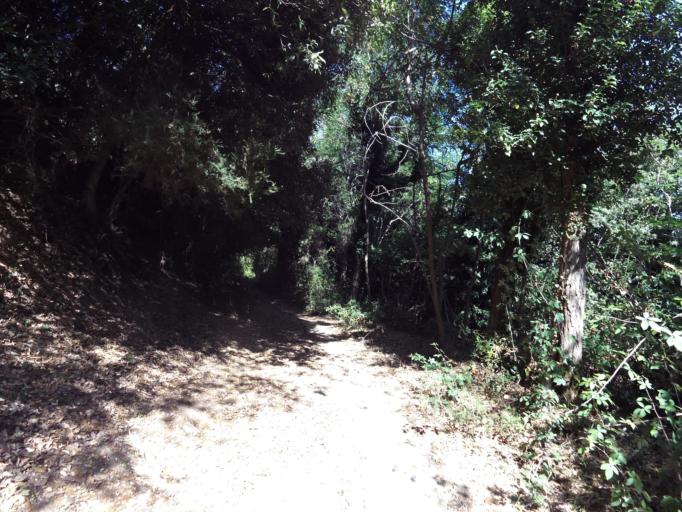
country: IT
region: Calabria
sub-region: Provincia di Reggio Calabria
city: Pazzano
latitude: 38.4707
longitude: 16.4142
